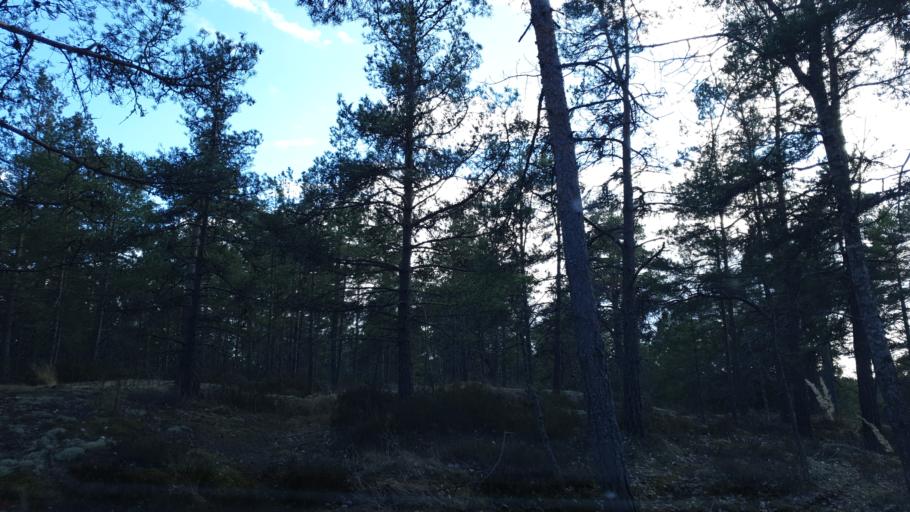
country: SE
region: Stockholm
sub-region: Varmdo Kommun
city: Holo
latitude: 59.2706
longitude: 18.6405
